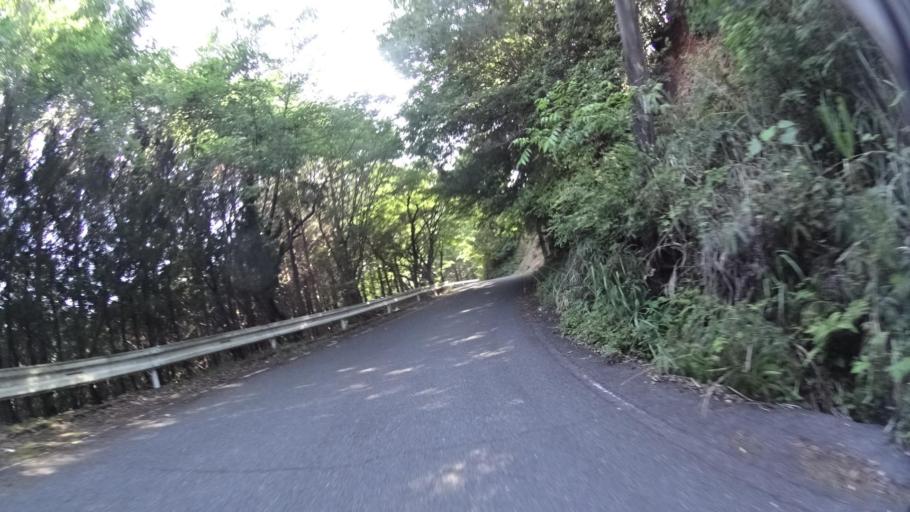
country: JP
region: Kyoto
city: Kameoka
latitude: 35.0009
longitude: 135.5624
